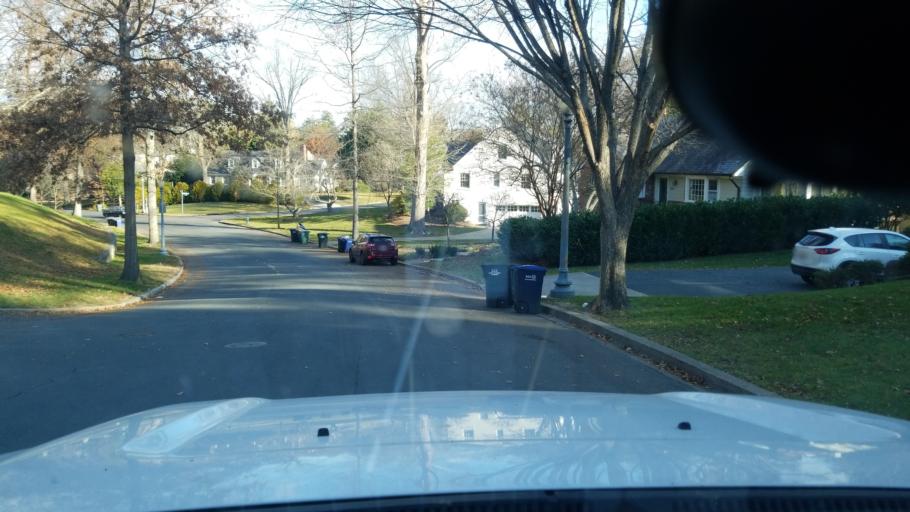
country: US
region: Maryland
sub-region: Montgomery County
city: Brookmont
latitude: 38.9416
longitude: -77.1021
